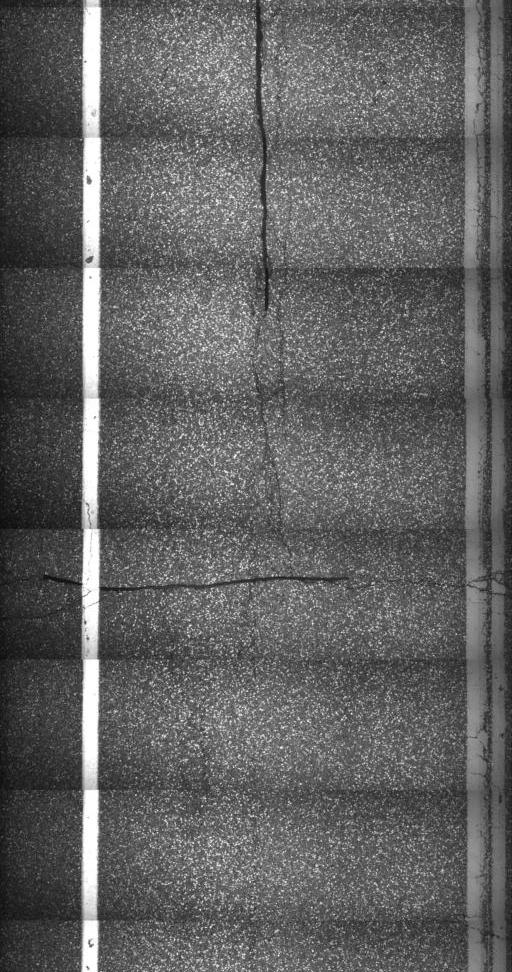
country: US
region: New Hampshire
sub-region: Grafton County
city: Lyme
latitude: 43.7805
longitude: -72.2062
